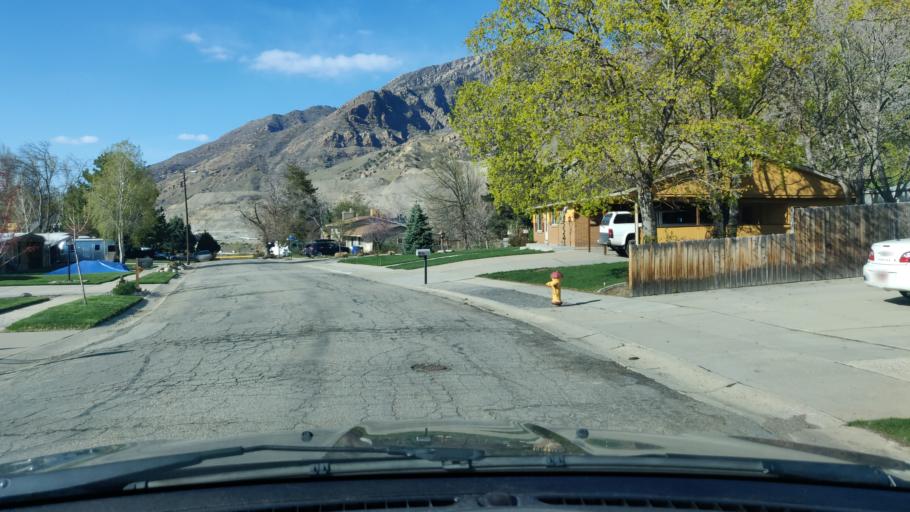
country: US
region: Utah
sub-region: Salt Lake County
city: Cottonwood Heights
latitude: 40.6184
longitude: -111.7944
